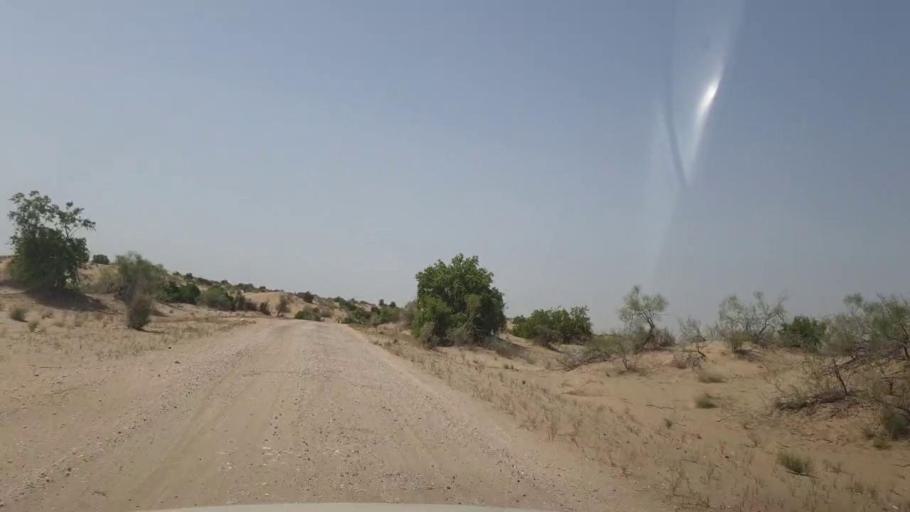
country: PK
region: Sindh
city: Khanpur
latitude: 27.4114
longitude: 69.3196
